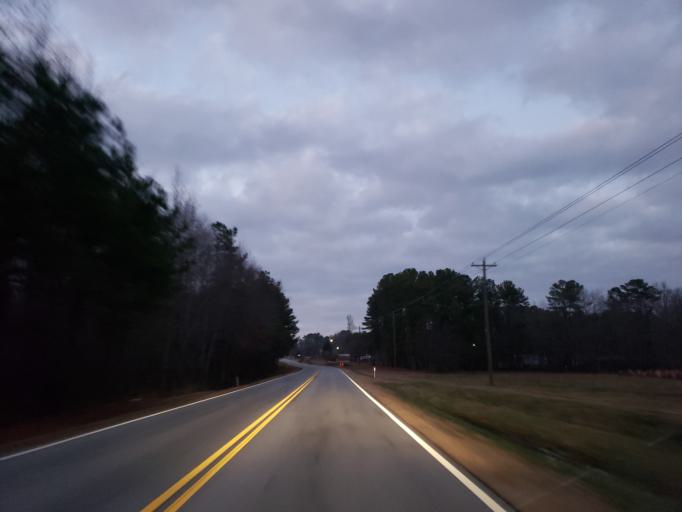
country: US
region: Georgia
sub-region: Carroll County
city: Temple
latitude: 33.7783
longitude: -85.0620
